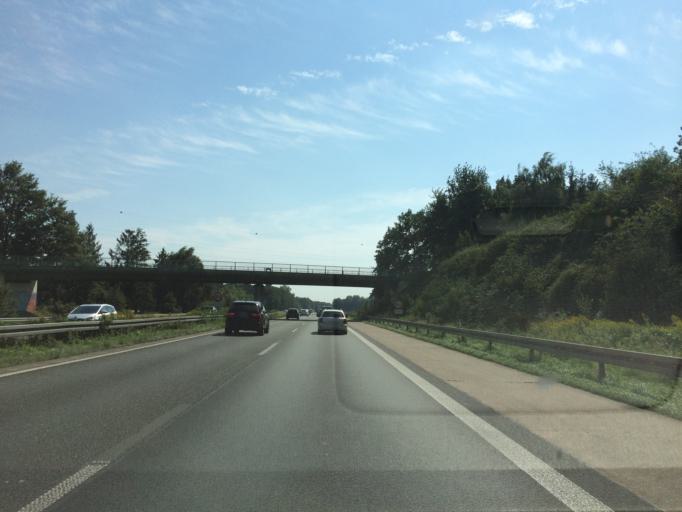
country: DE
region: North Rhine-Westphalia
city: Werne
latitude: 51.6510
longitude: 7.6838
